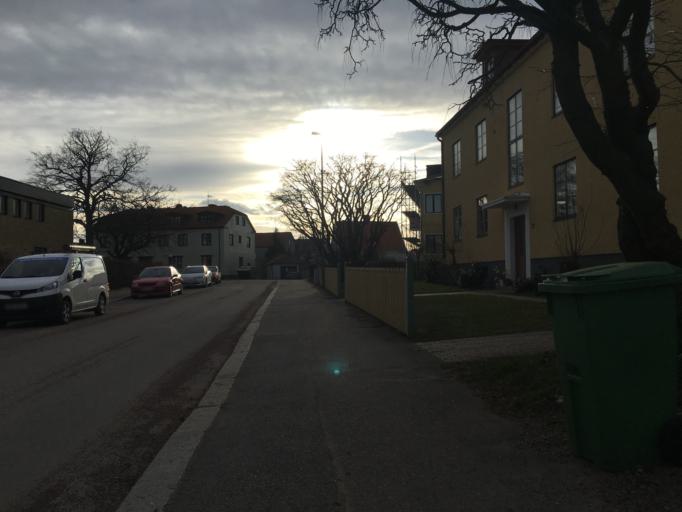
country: SE
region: Kalmar
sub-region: Kalmar Kommun
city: Kalmar
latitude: 56.6565
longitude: 16.3404
